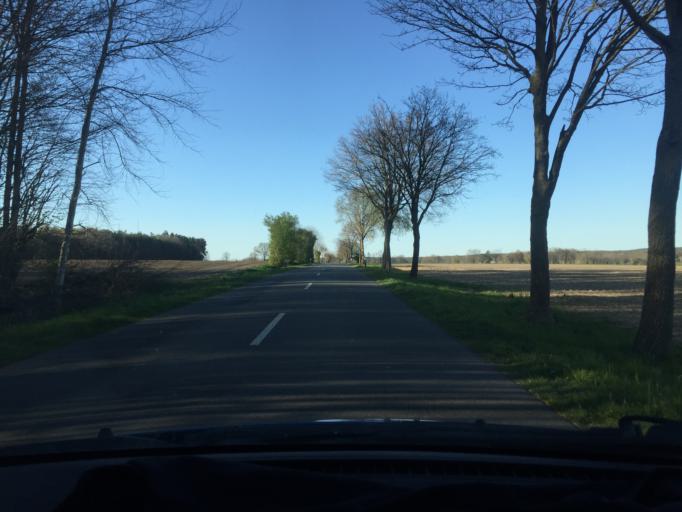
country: DE
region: Lower Saxony
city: Himbergen
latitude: 53.0745
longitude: 10.7294
